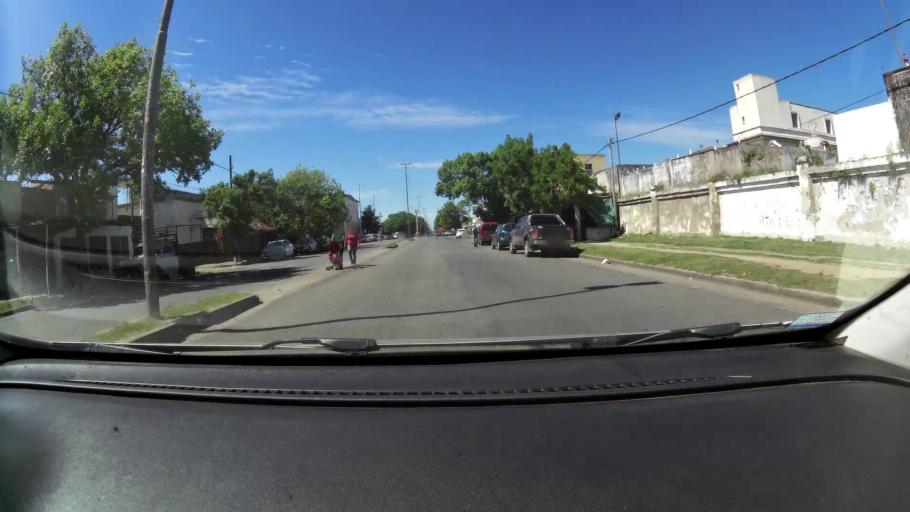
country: AR
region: Santa Fe
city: Perez
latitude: -32.9600
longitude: -60.7119
